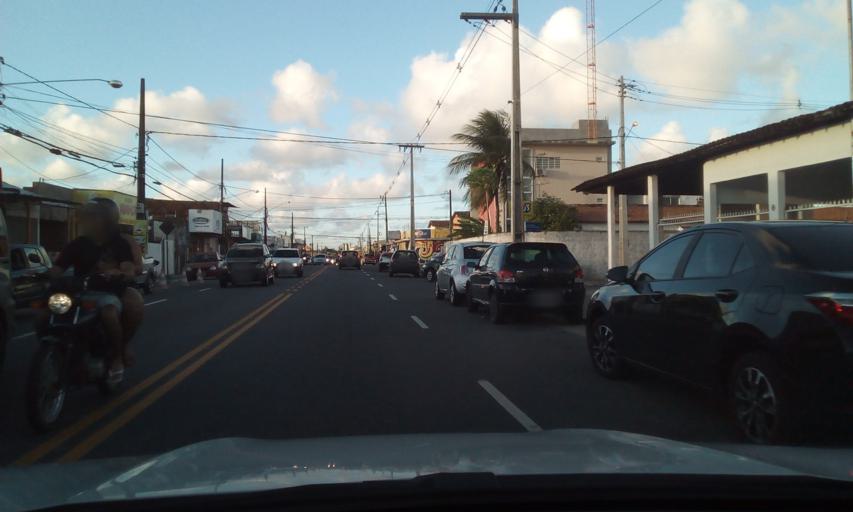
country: BR
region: Paraiba
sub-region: Joao Pessoa
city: Joao Pessoa
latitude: -7.1679
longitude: -34.8422
